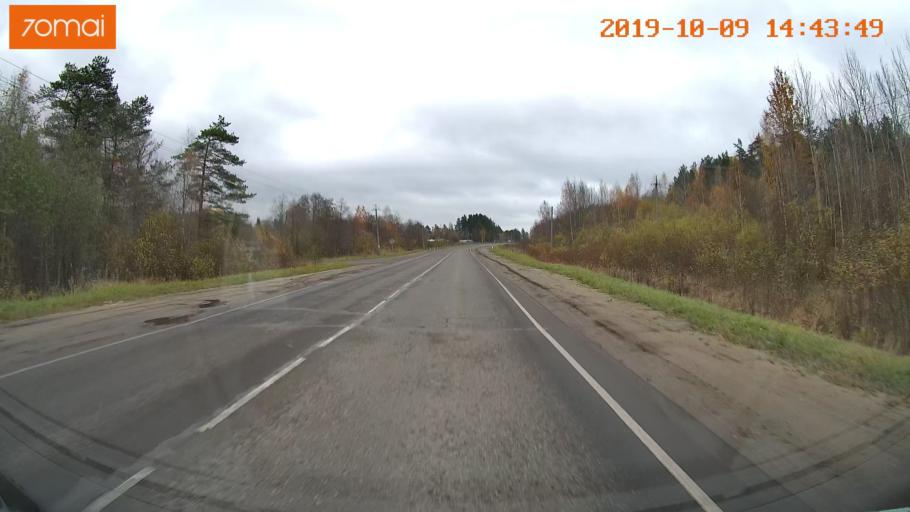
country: RU
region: Kostroma
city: Buy
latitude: 58.4559
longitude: 41.5522
